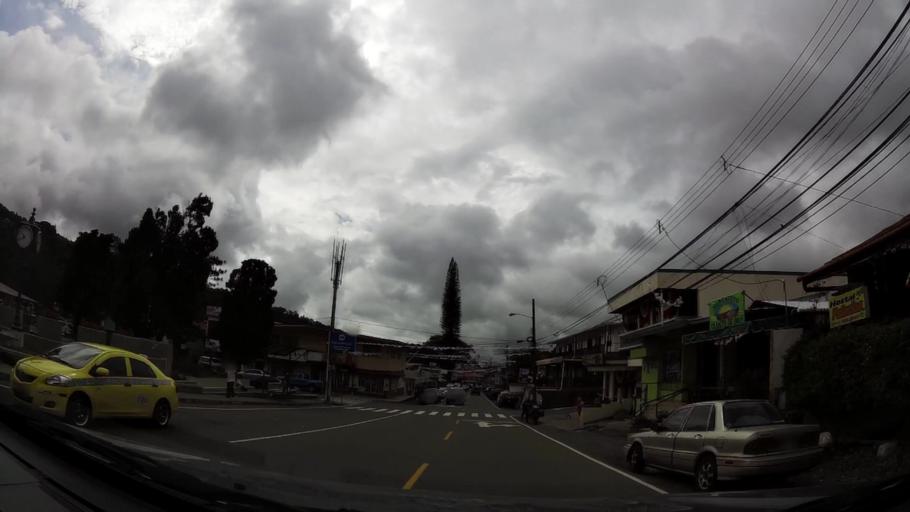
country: PA
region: Chiriqui
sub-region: Distrito Boquete
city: Boquete
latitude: 8.7765
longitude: -82.4326
